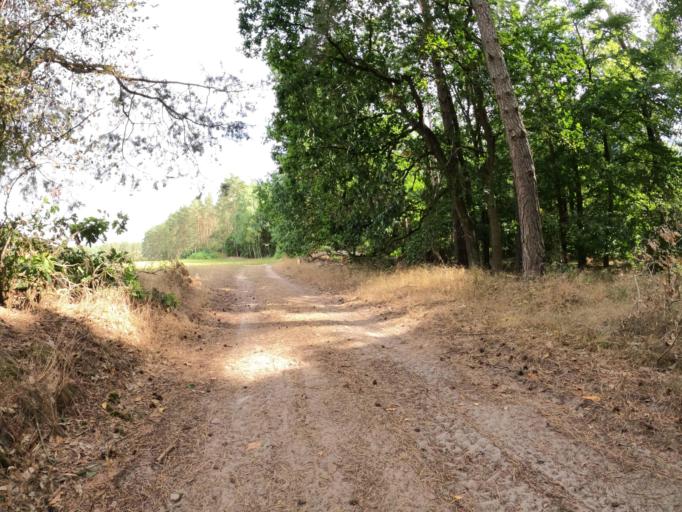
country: DE
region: Brandenburg
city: Lychen
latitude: 53.2752
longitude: 13.4356
